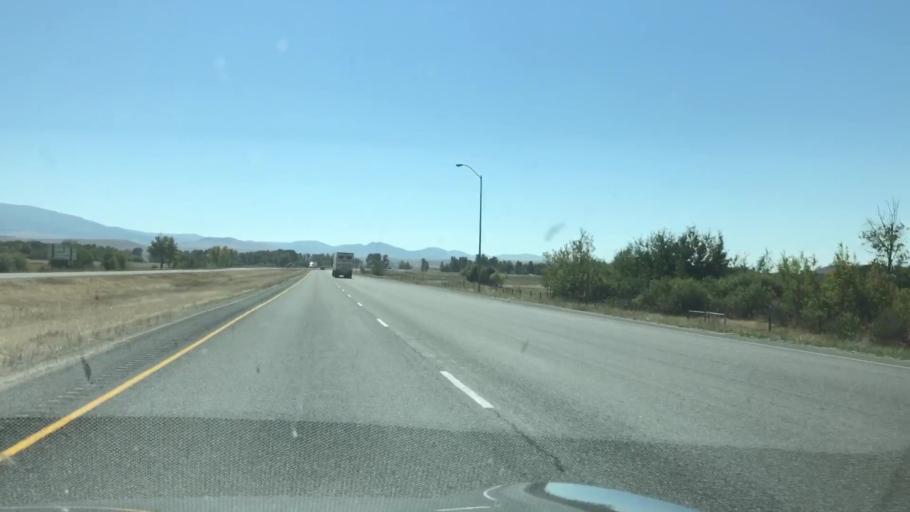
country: US
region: Montana
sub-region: Powell County
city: Deer Lodge
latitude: 46.4070
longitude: -112.7262
